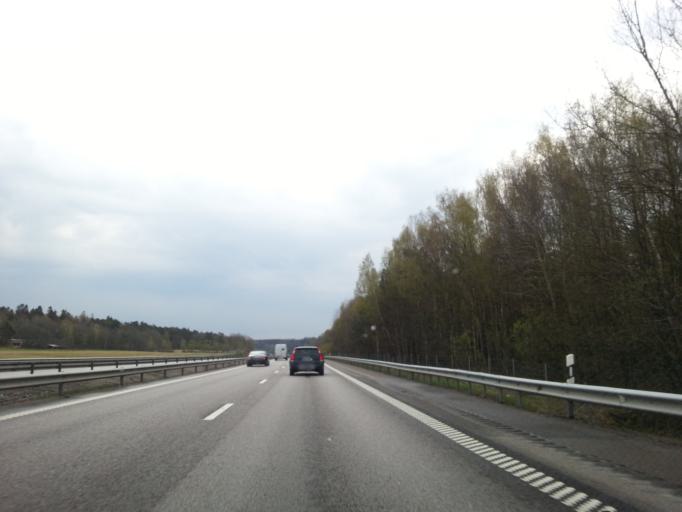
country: SE
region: Halland
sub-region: Kungsbacka Kommun
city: Kungsbacka
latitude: 57.4431
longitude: 12.1136
